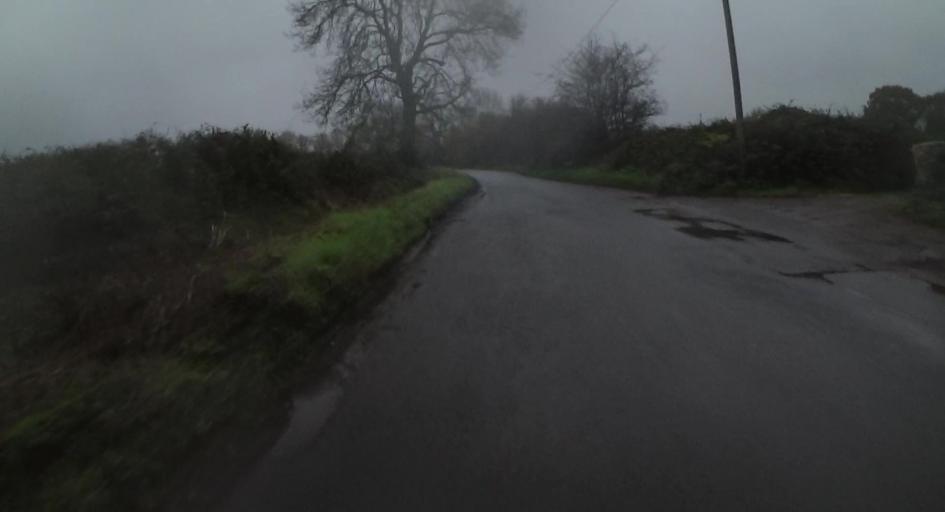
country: GB
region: England
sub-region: Wokingham
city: Swallowfield
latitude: 51.3742
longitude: -0.9545
